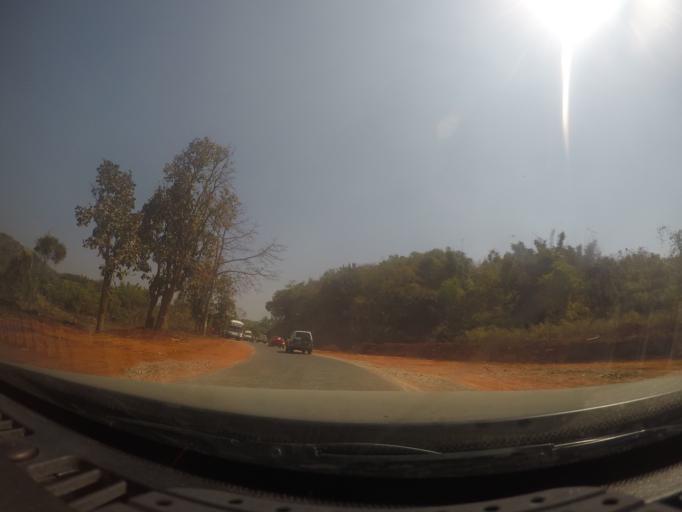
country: MM
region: Shan
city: Taunggyi
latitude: 20.7781
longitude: 97.1431
